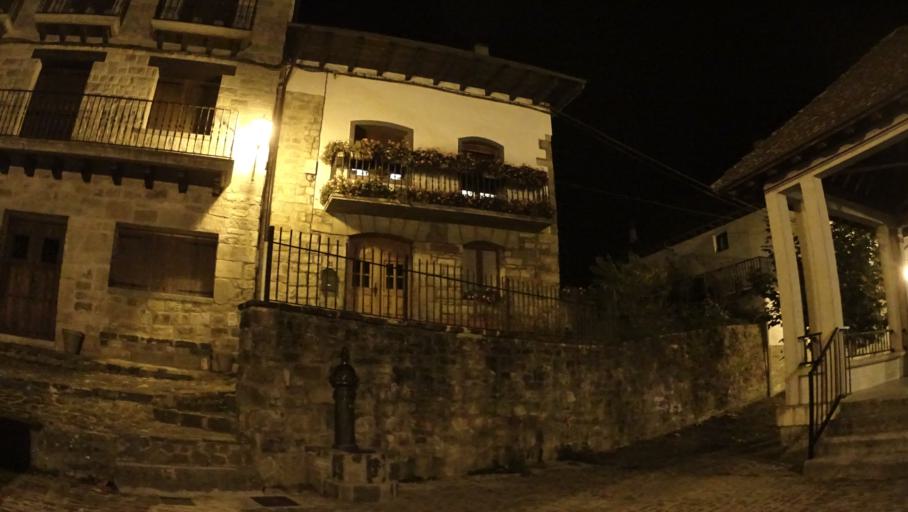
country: ES
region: Navarre
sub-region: Provincia de Navarra
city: Oronz
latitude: 42.8868
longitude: -1.0965
